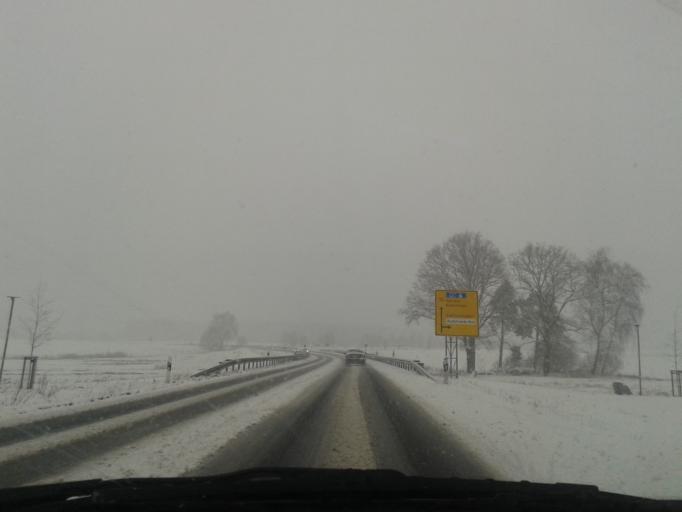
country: DE
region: Saxony
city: Rammenau
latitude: 51.1451
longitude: 14.1556
